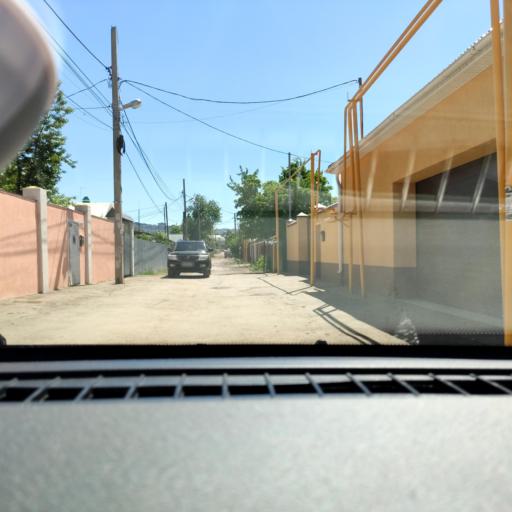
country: RU
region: Samara
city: Samara
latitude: 53.2718
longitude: 50.2012
